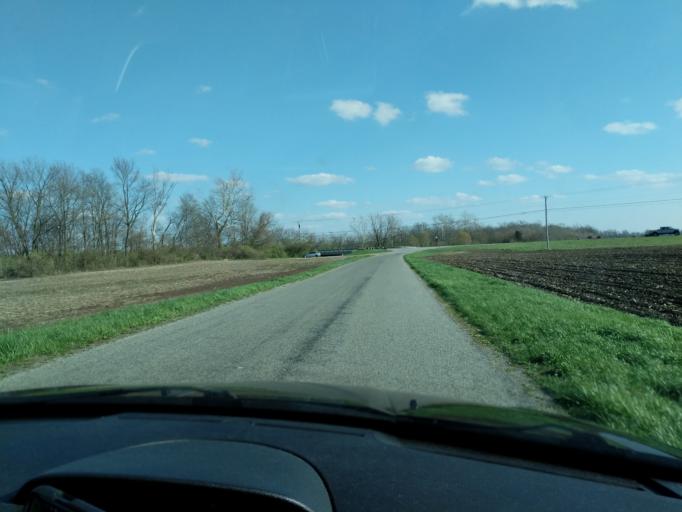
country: US
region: Ohio
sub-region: Champaign County
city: Urbana
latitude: 40.1087
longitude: -83.8006
